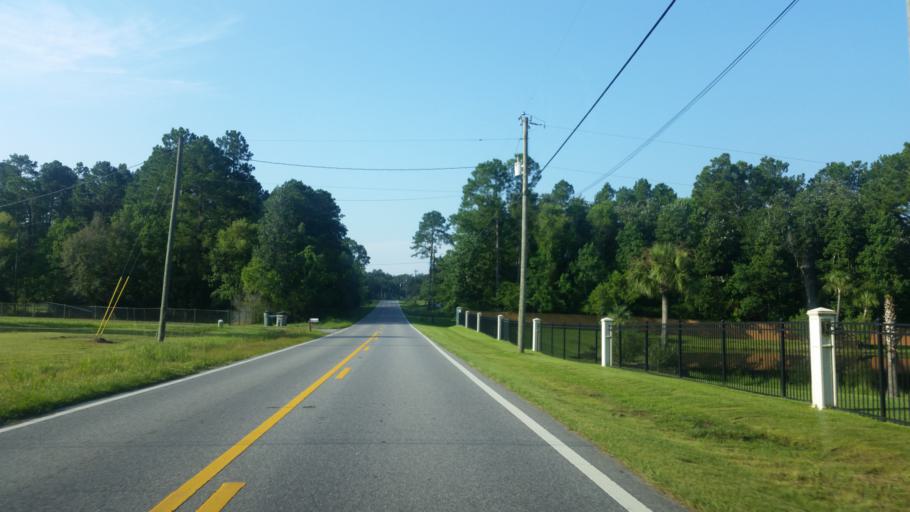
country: US
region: Florida
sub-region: Escambia County
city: Bellview
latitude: 30.5102
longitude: -87.3224
